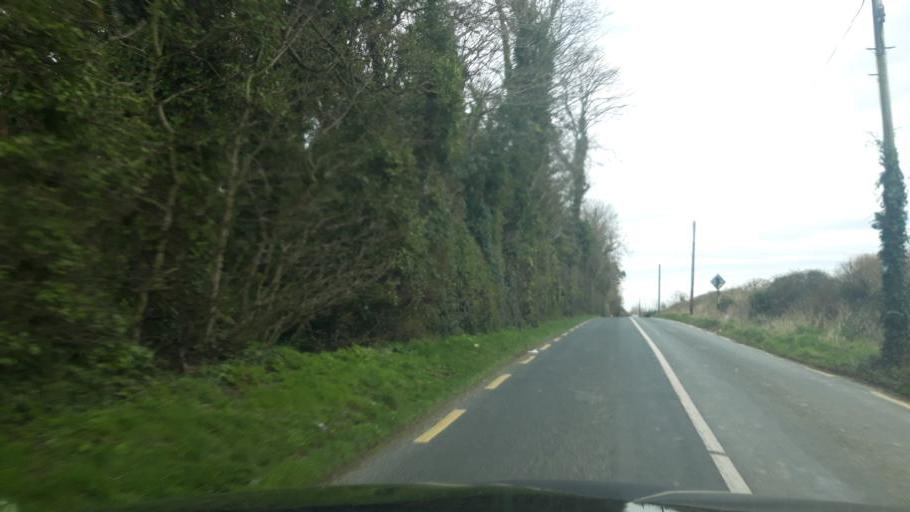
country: IE
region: Leinster
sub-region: Kildare
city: Maynooth
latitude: 53.3540
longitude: -6.6213
